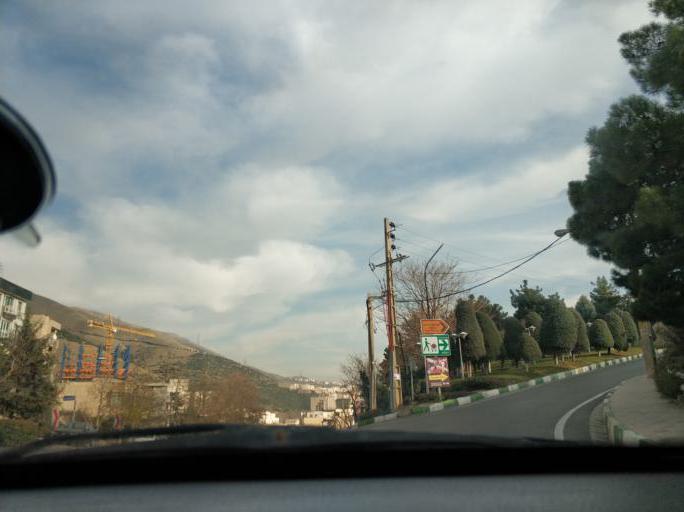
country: IR
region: Tehran
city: Tajrish
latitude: 35.8165
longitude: 51.4856
